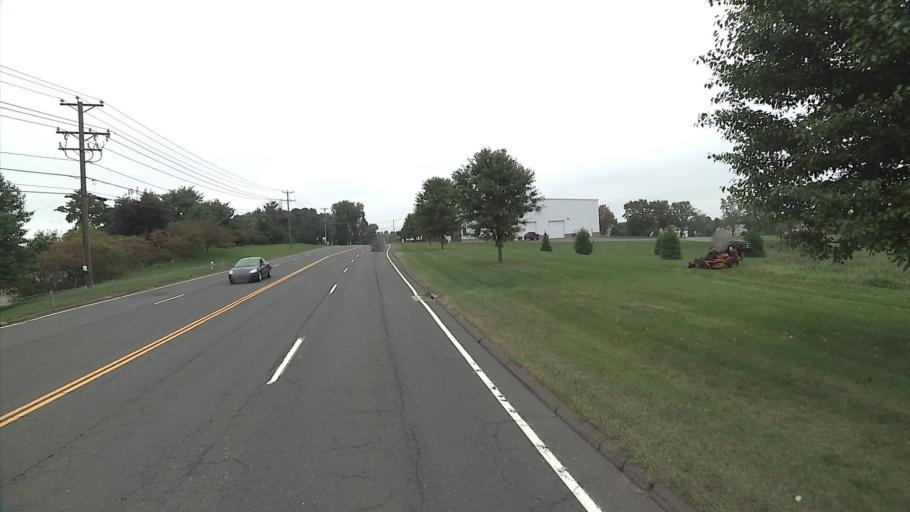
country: US
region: Connecticut
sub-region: Hartford County
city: Suffield Depot
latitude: 41.9605
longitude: -72.6627
